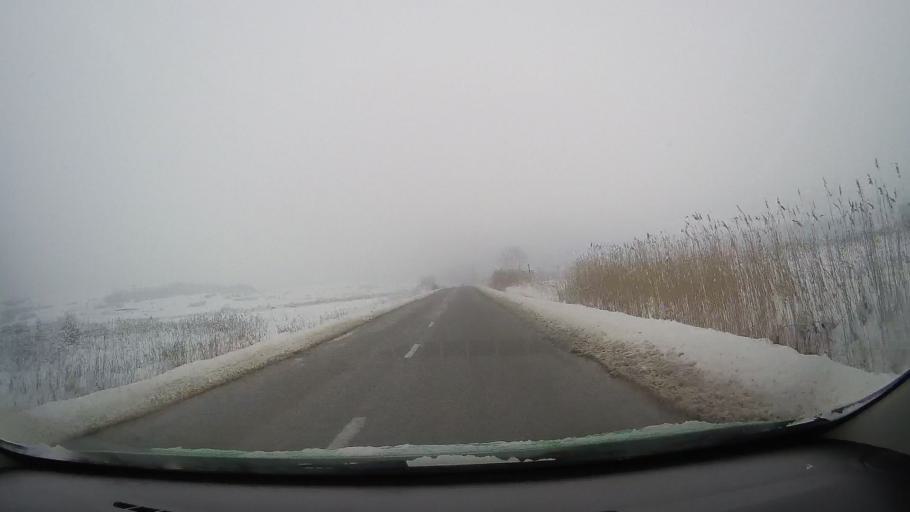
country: RO
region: Sibiu
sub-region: Comuna Orlat
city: Orlat
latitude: 45.7804
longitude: 23.9450
